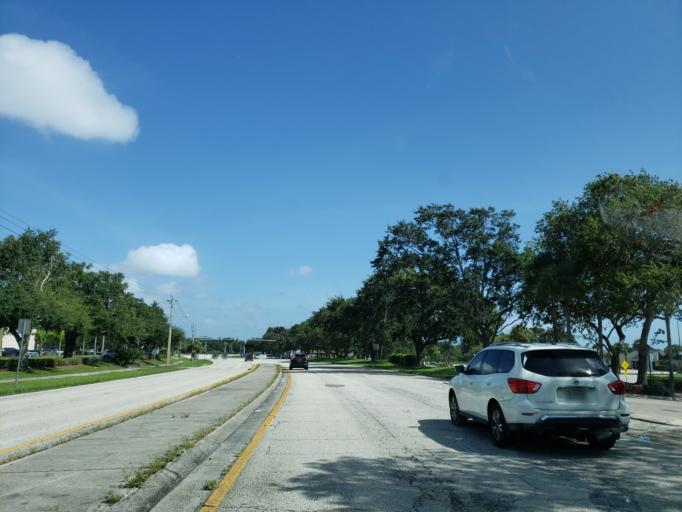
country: US
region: Florida
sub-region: Brevard County
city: West Melbourne
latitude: 28.0801
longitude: -80.6535
